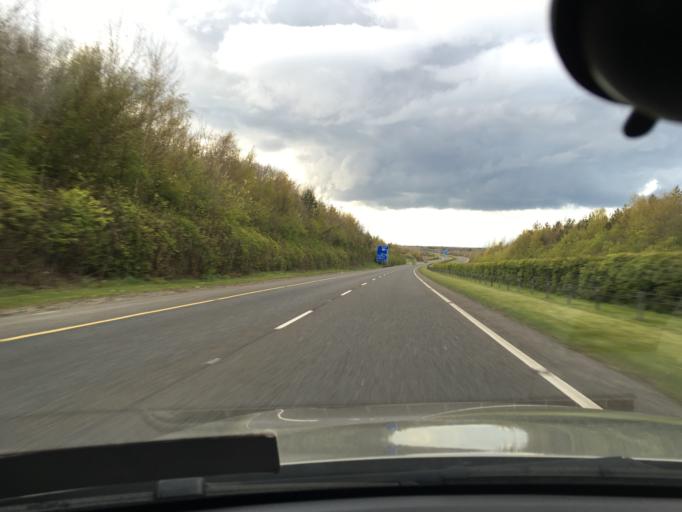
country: IE
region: Leinster
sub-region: An Mhi
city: Stamullin
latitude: 53.6242
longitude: -6.2483
